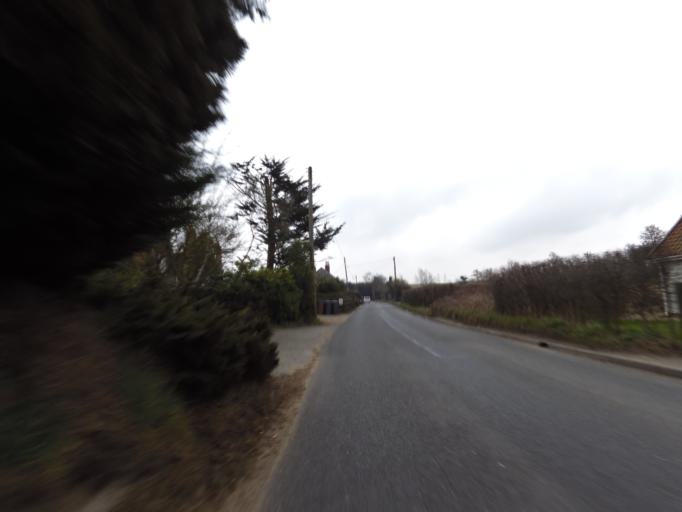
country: GB
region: England
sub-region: Suffolk
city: Wickham Market
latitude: 52.1587
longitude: 1.3838
